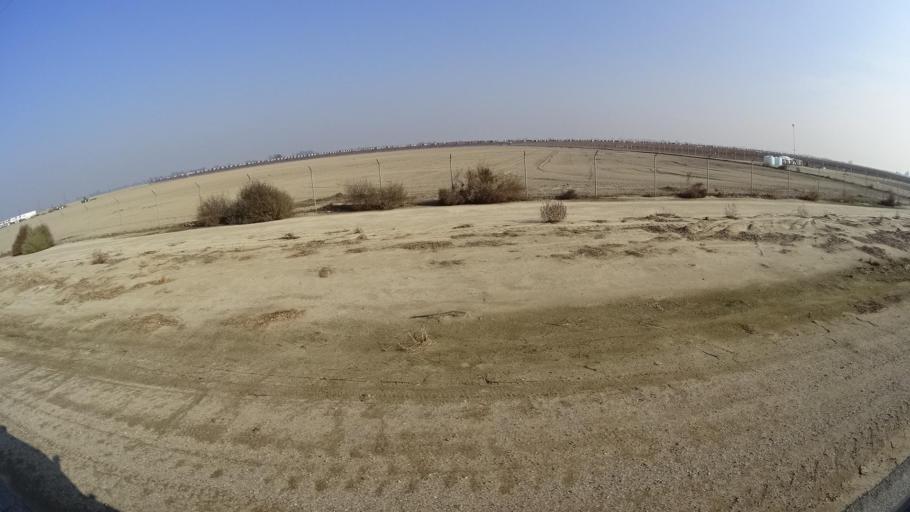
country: US
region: California
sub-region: Kern County
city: Greenfield
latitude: 35.2201
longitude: -119.0391
